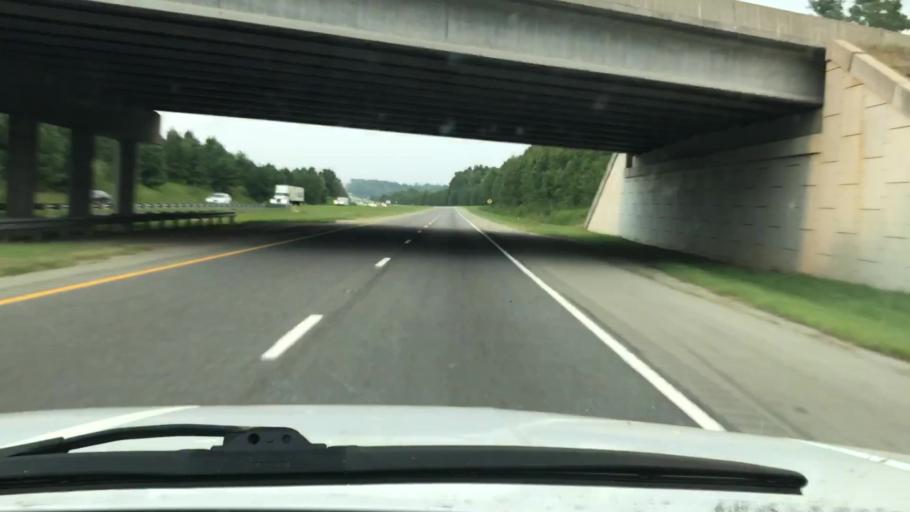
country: US
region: Virginia
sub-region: Henrico County
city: Short Pump
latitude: 37.5590
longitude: -77.6901
